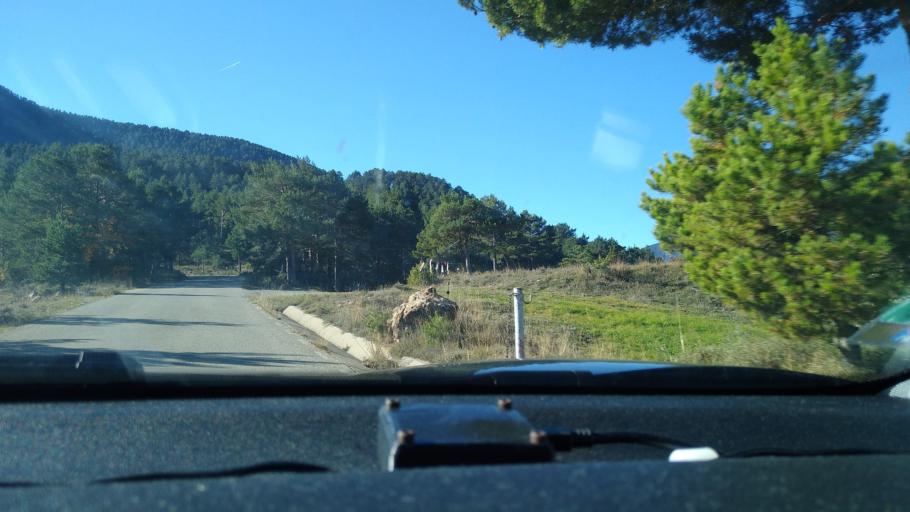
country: ES
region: Catalonia
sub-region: Provincia de Barcelona
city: Saldes
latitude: 42.2148
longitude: 1.7180
